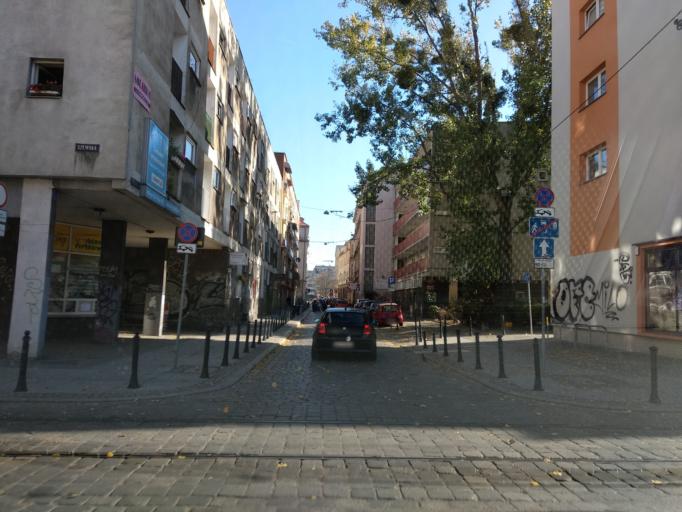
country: PL
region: Lower Silesian Voivodeship
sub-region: Powiat wroclawski
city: Wroclaw
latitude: 51.1121
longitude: 17.0355
